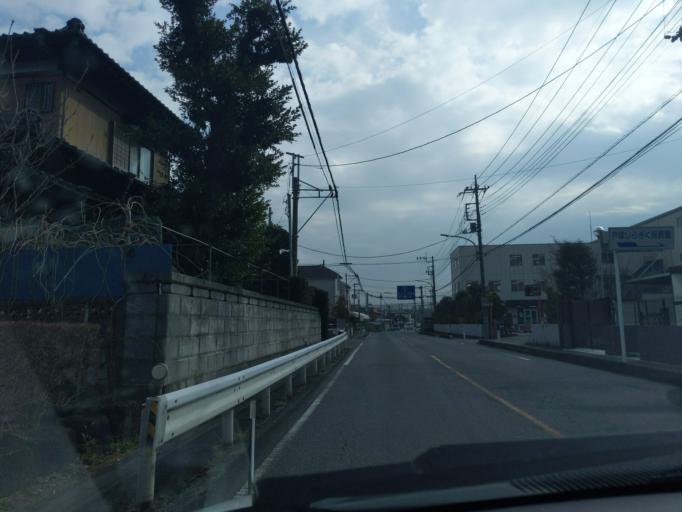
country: JP
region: Saitama
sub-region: Kawaguchi-shi
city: Hatogaya-honcho
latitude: 35.8563
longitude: 139.7534
